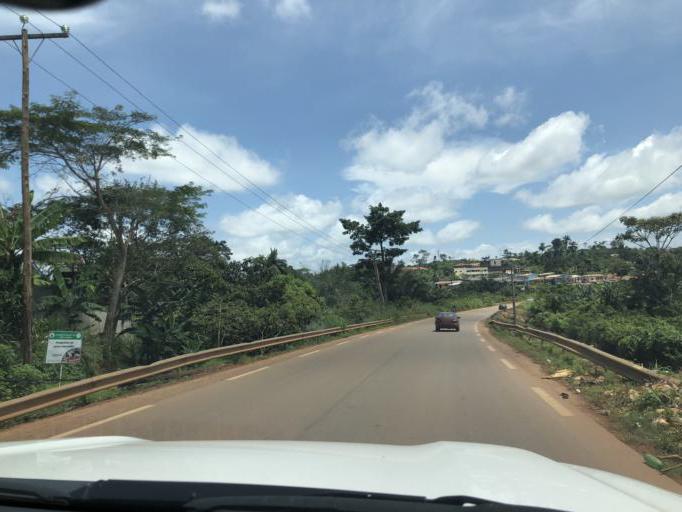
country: CM
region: Centre
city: Yaounde
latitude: 3.8641
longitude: 11.6164
